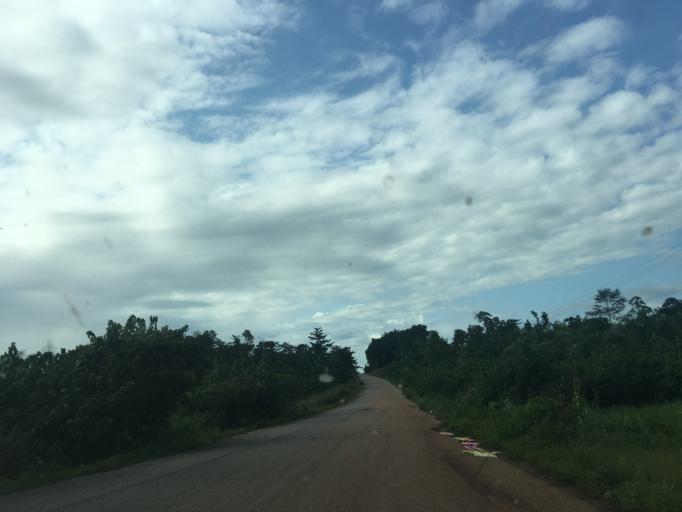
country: GH
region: Western
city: Wassa-Akropong
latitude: 5.9875
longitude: -2.4127
